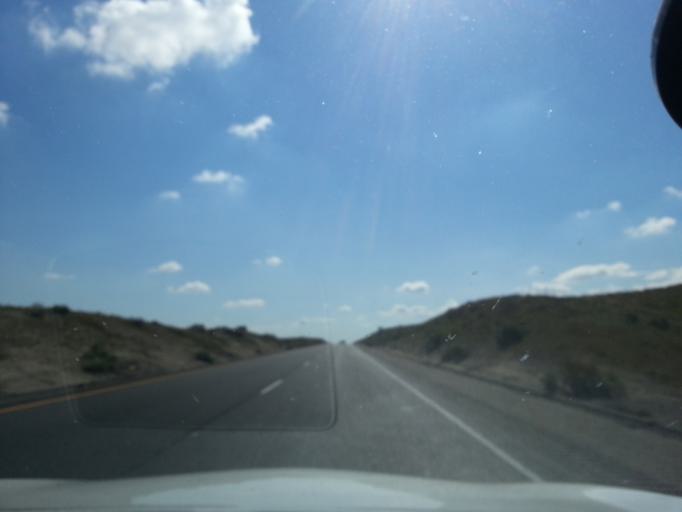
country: US
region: California
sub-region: Fresno County
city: Mendota
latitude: 36.4890
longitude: -120.4437
